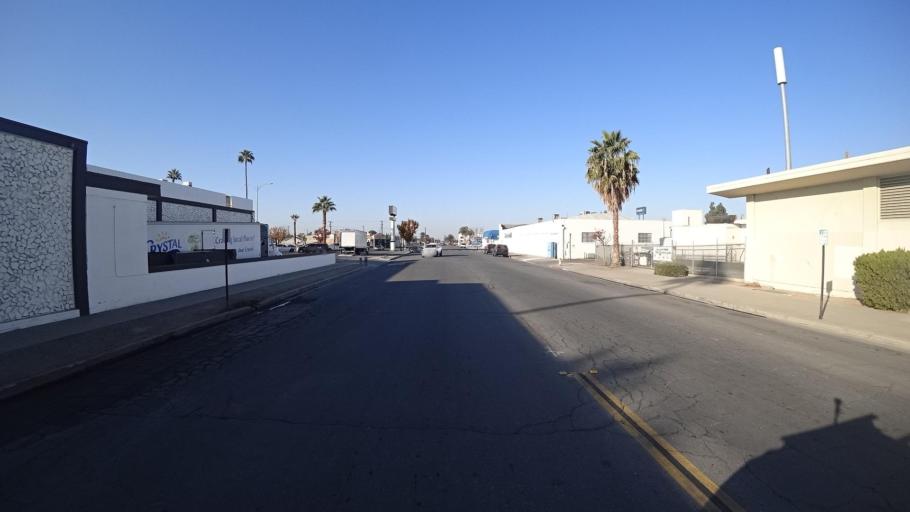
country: US
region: California
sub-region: Kern County
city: Delano
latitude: 35.7679
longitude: -119.2444
